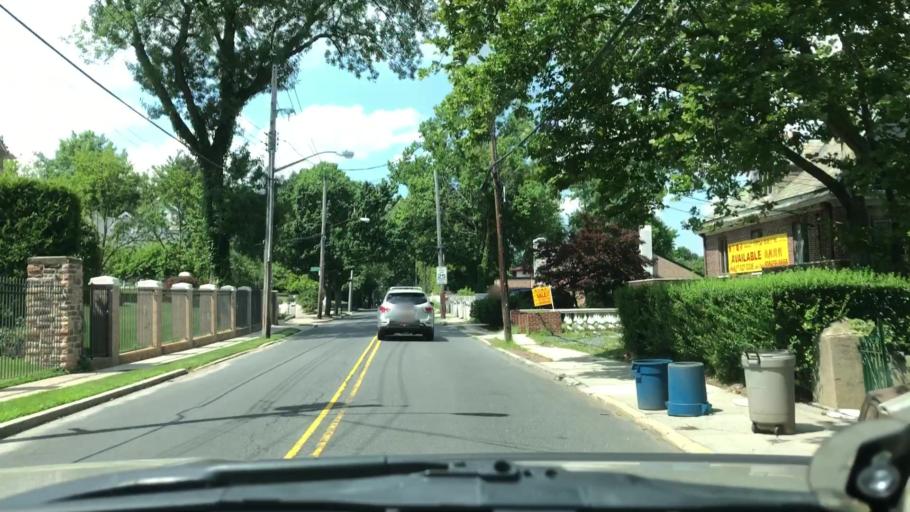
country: US
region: New Jersey
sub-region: Hudson County
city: Bayonne
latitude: 40.6237
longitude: -74.0885
